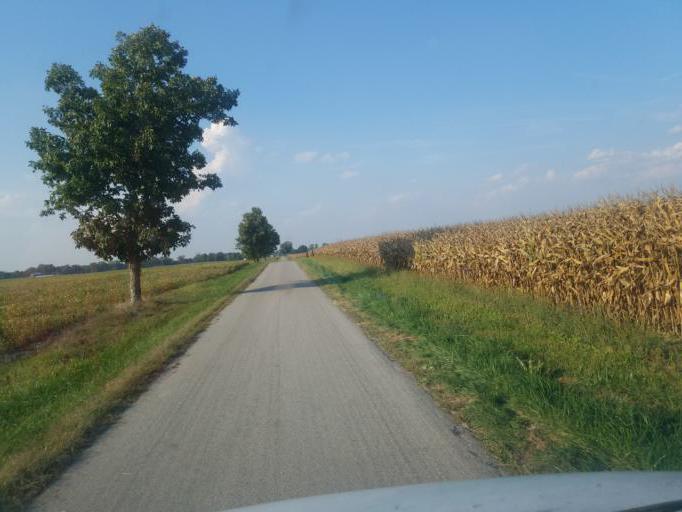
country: US
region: Ohio
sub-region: Wyandot County
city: Upper Sandusky
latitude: 40.9222
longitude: -83.1893
